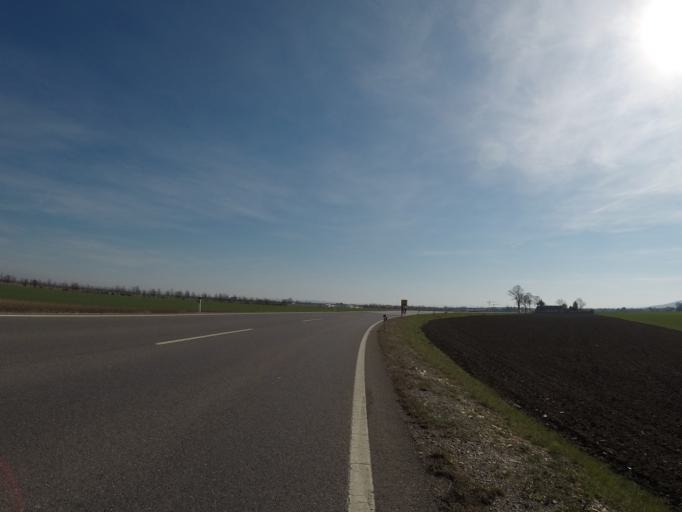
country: AT
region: Lower Austria
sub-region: Politischer Bezirk Modling
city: Vosendorf
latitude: 48.1277
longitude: 16.3562
